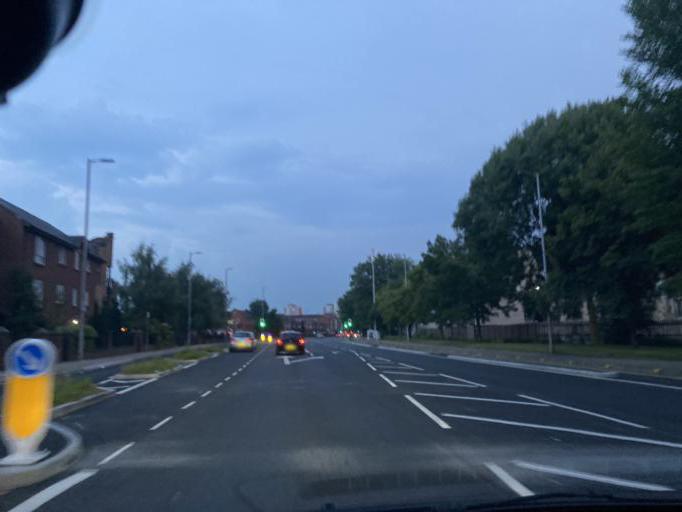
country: GB
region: England
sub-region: Manchester
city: Hulme
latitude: 53.4687
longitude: -2.2578
